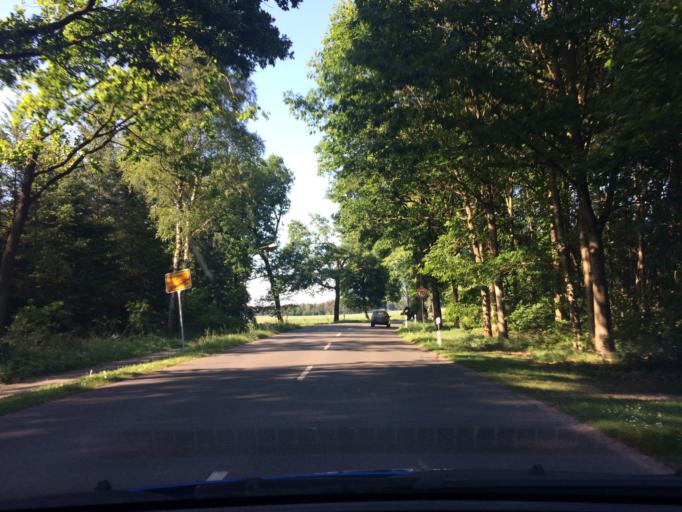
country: DE
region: Lower Saxony
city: Bispingen
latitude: 53.0345
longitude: 9.9275
